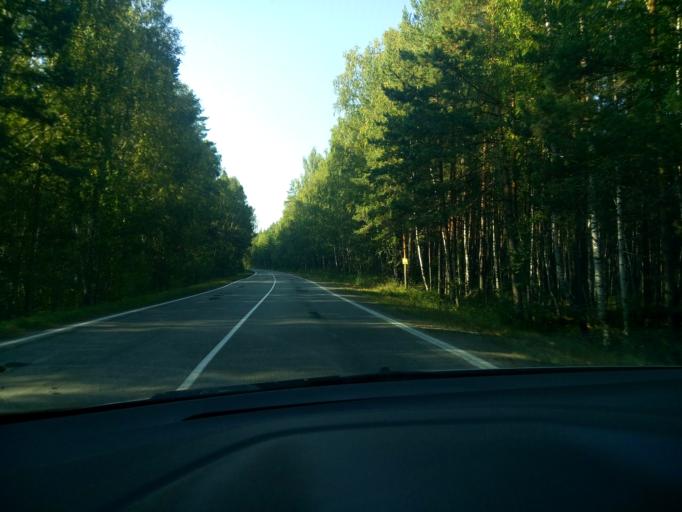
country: RU
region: Chelyabinsk
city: Ozersk
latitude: 55.8412
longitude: 60.6521
